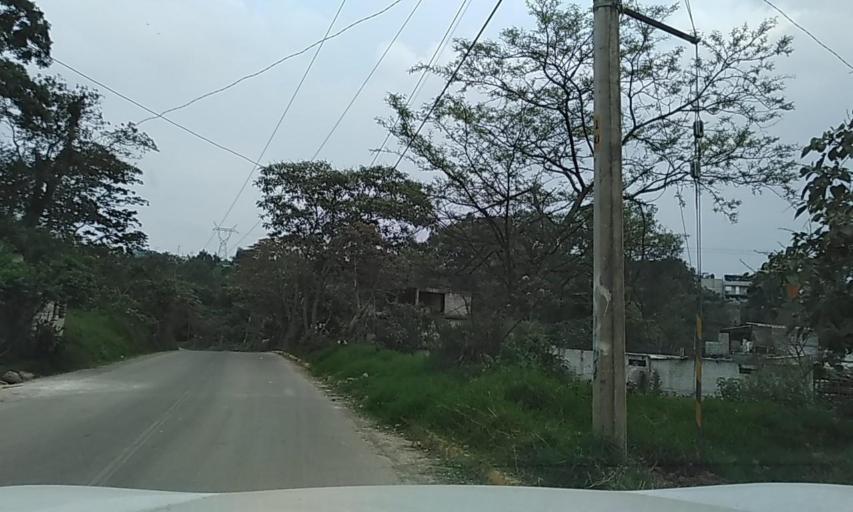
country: MX
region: Veracruz
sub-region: Jilotepec
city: El Pueblito (Garbanzal)
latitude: 19.5735
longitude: -96.8944
